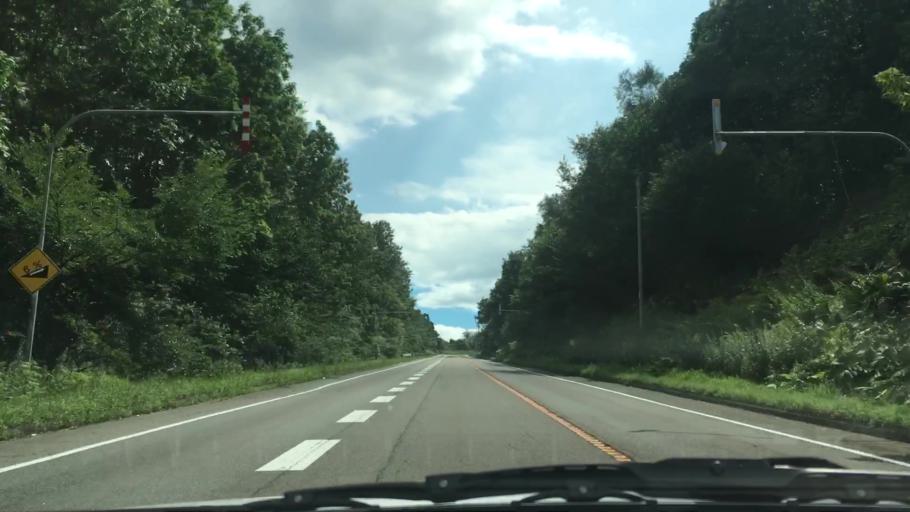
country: JP
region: Hokkaido
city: Otofuke
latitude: 43.2815
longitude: 143.4064
